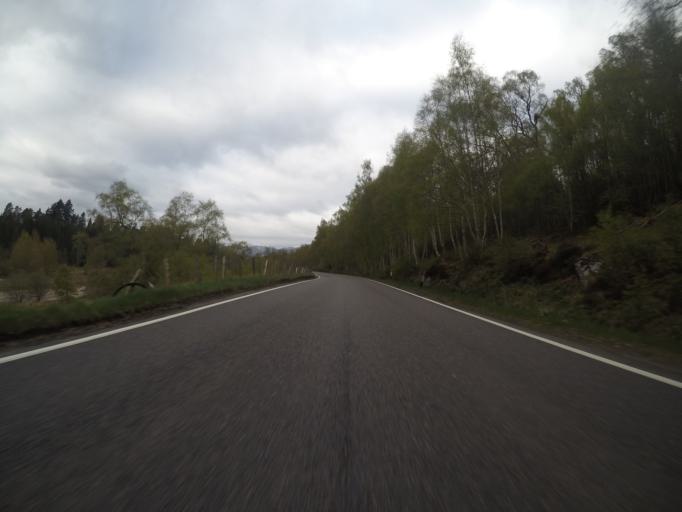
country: GB
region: Scotland
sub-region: Highland
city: Kingussie
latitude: 56.9760
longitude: -4.3987
